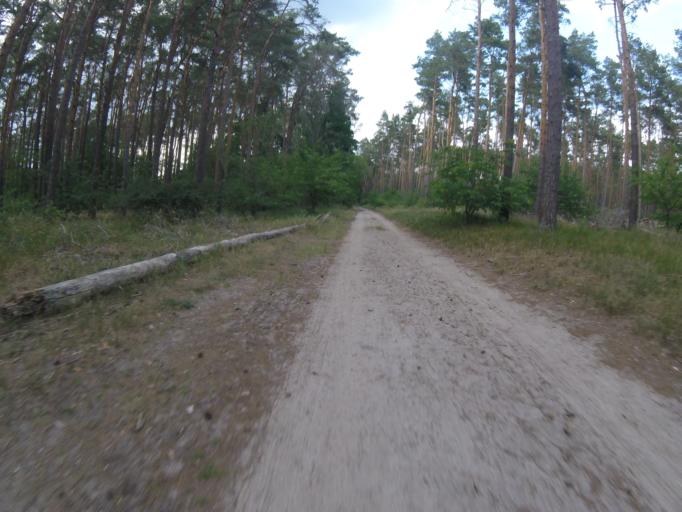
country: DE
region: Brandenburg
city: Konigs Wusterhausen
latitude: 52.2684
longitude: 13.6094
